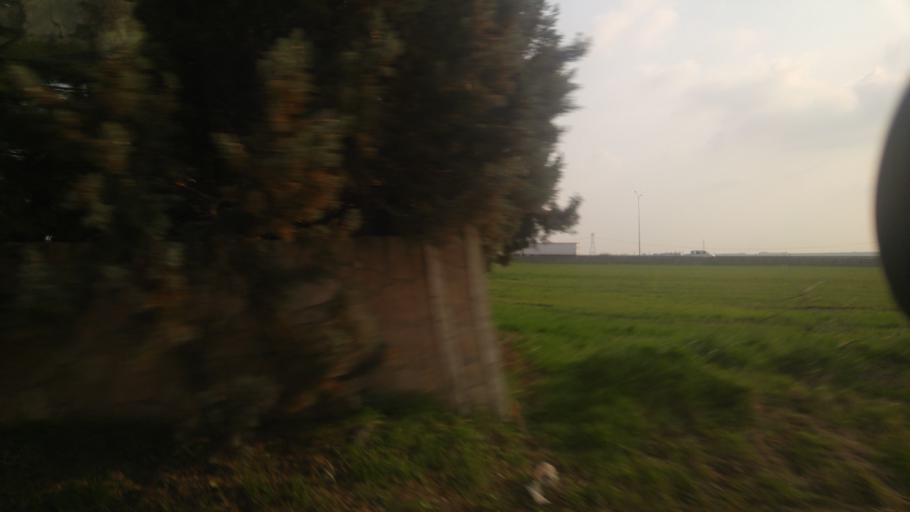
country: TR
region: Istanbul
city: Kavakli
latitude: 41.1077
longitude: 28.2945
